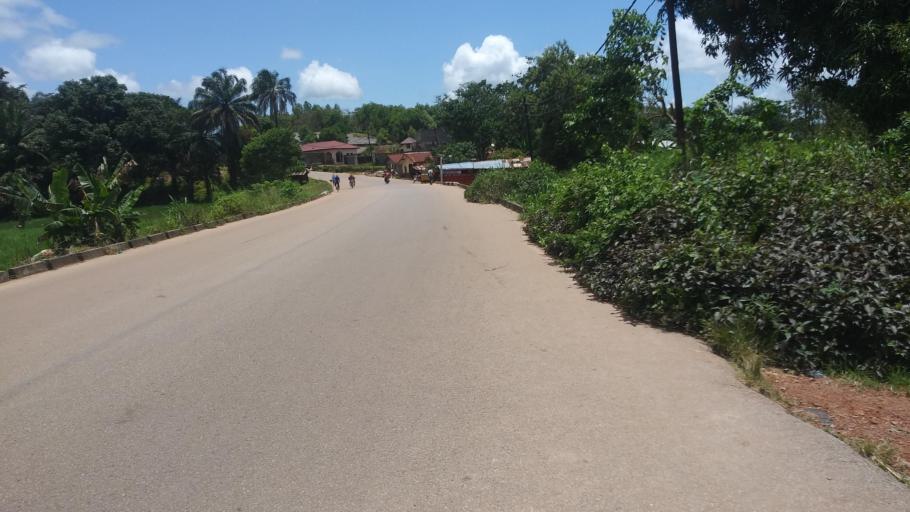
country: SL
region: Northern Province
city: Makeni
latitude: 8.8792
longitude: -12.0288
